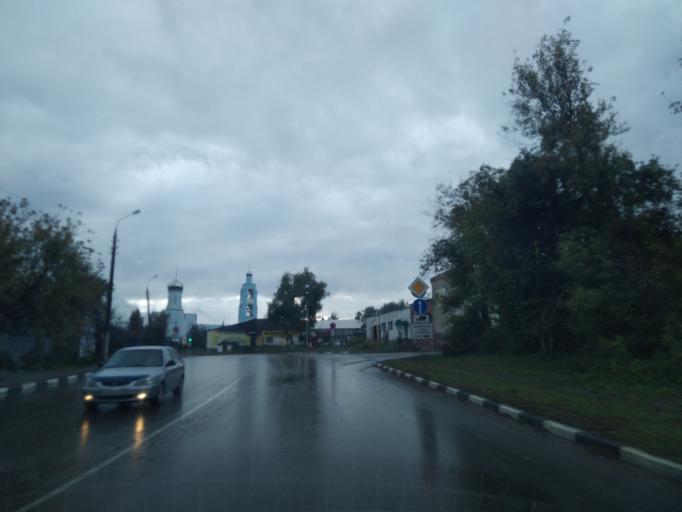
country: RU
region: Tula
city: Yefremov
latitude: 53.1365
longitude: 38.1160
